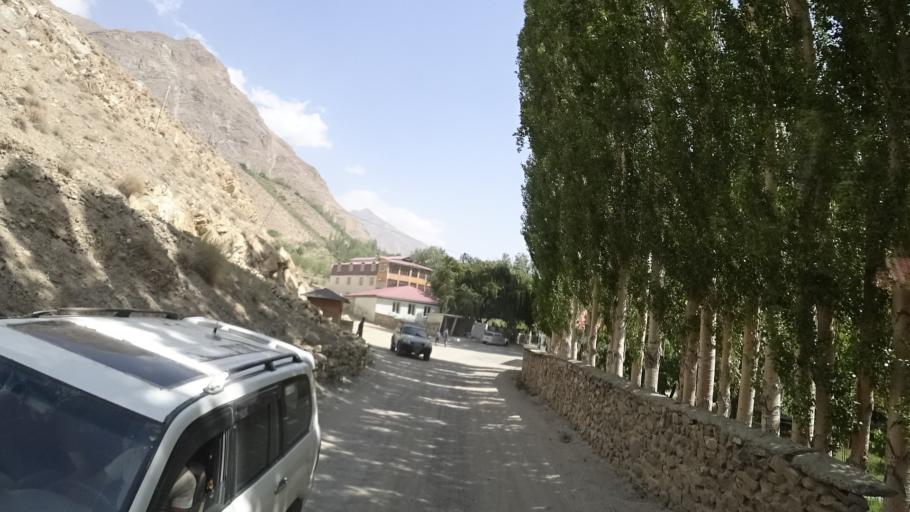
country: TJ
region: Gorno-Badakhshan
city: Ishqoshim
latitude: 36.9268
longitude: 71.4932
